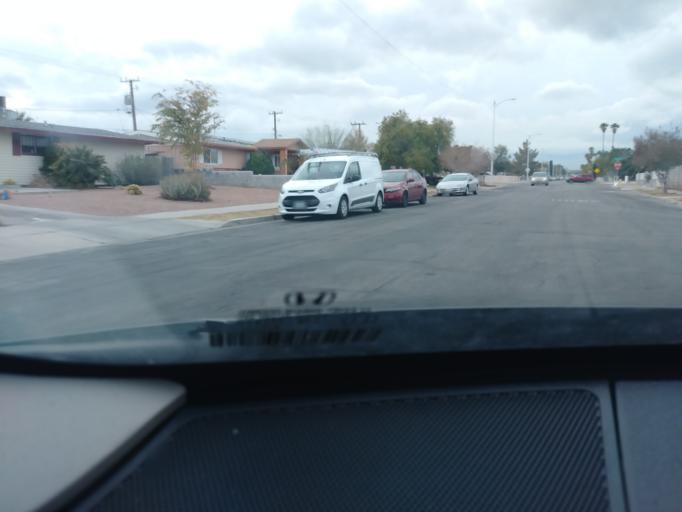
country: US
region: Nevada
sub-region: Clark County
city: Spring Valley
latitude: 36.1632
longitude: -115.2183
